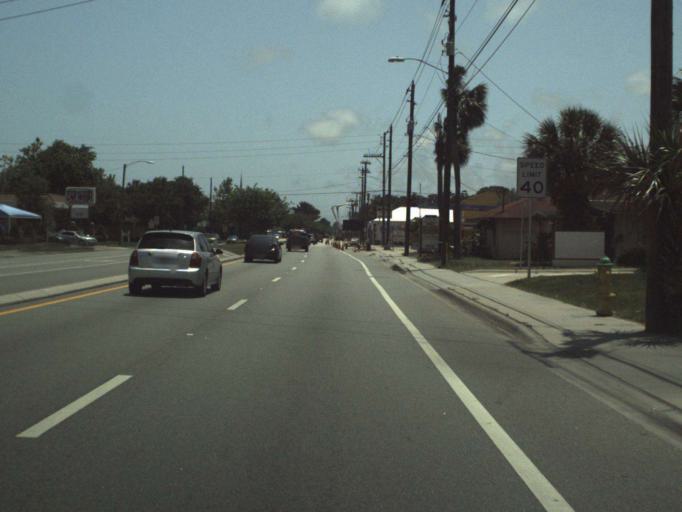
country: US
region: Florida
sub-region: Volusia County
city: Ormond Beach
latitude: 29.2823
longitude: -81.0618
